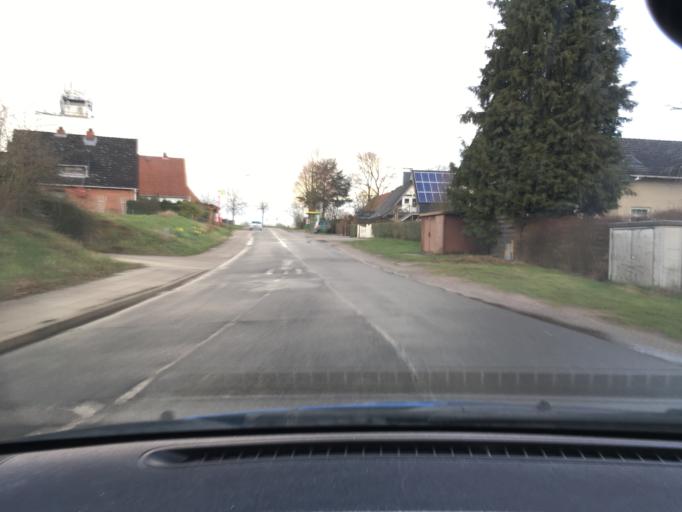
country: DE
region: Lower Saxony
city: Harmstorf
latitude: 53.3768
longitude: 9.9906
